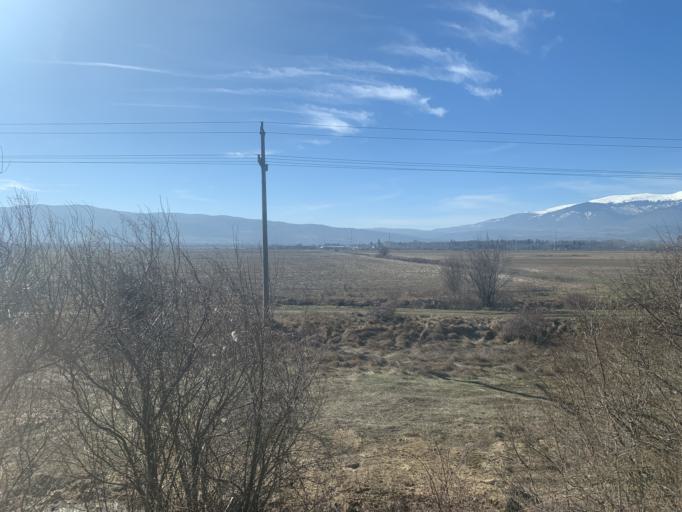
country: BG
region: Sofia-Capital
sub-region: Stolichna Obshtina
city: Sofia
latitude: 42.6571
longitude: 23.4474
